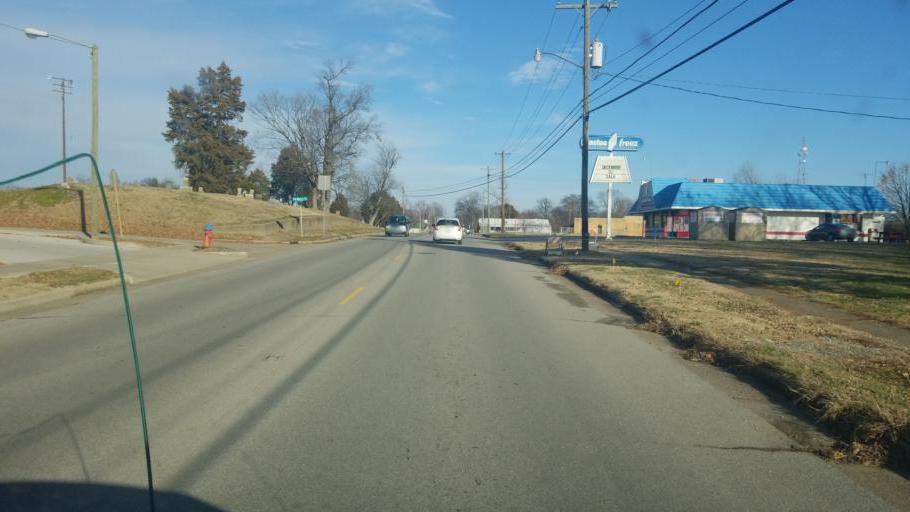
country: US
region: Illinois
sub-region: Wabash County
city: Mount Carmel
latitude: 38.4040
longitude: -87.7720
